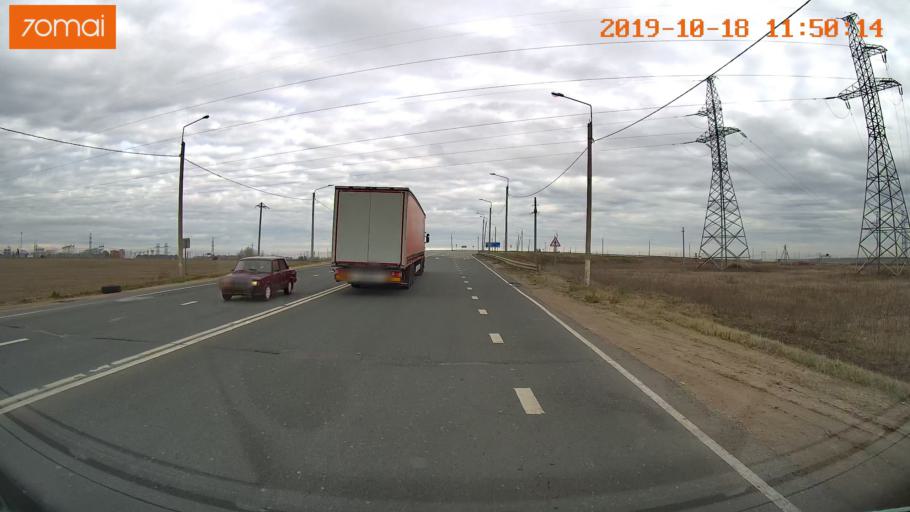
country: RU
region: Rjazan
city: Mikhaylov
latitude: 54.2592
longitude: 39.0019
